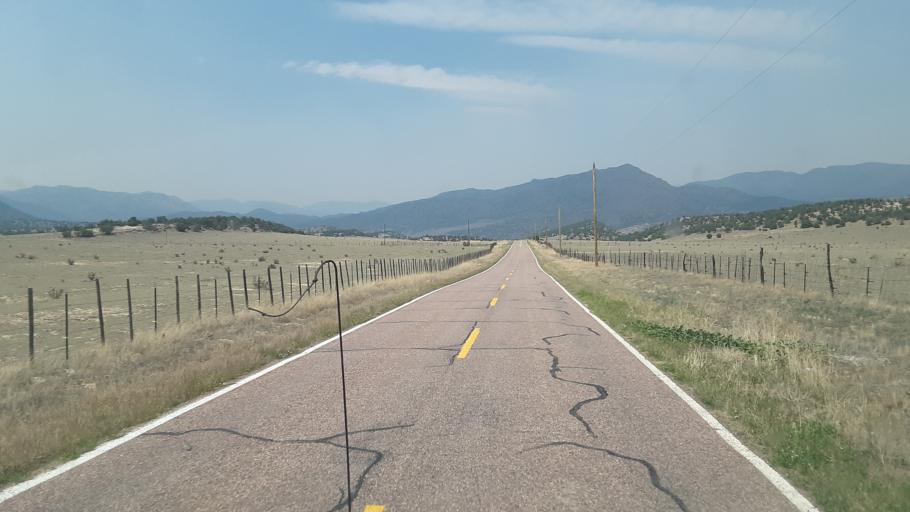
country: US
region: Colorado
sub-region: Fremont County
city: Canon City
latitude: 38.4602
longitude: -105.3759
